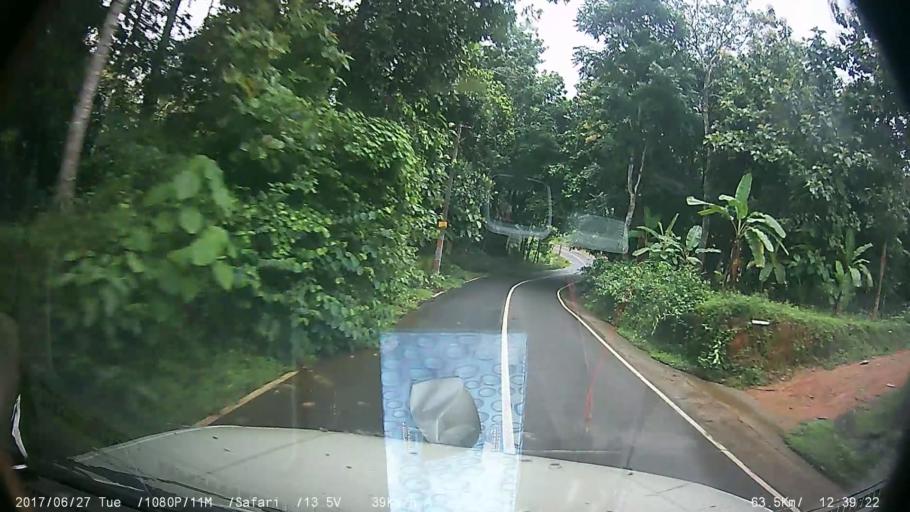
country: IN
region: Kerala
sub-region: Kottayam
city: Palackattumala
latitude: 9.7772
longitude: 76.5429
